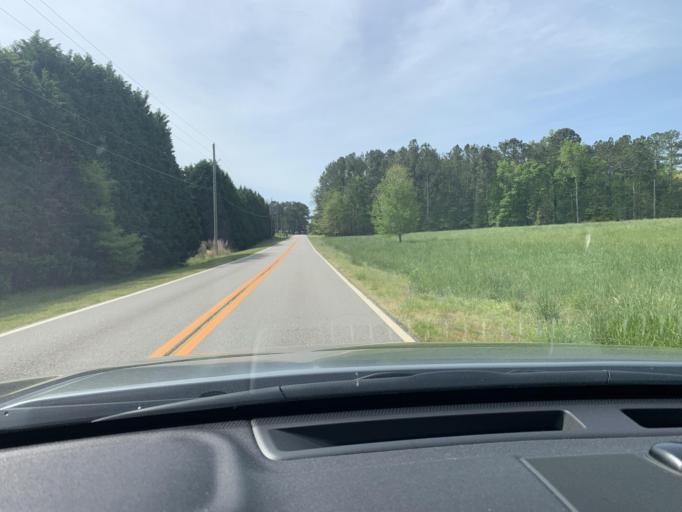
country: US
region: Georgia
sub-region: Oconee County
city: Watkinsville
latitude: 33.8355
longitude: -83.4875
